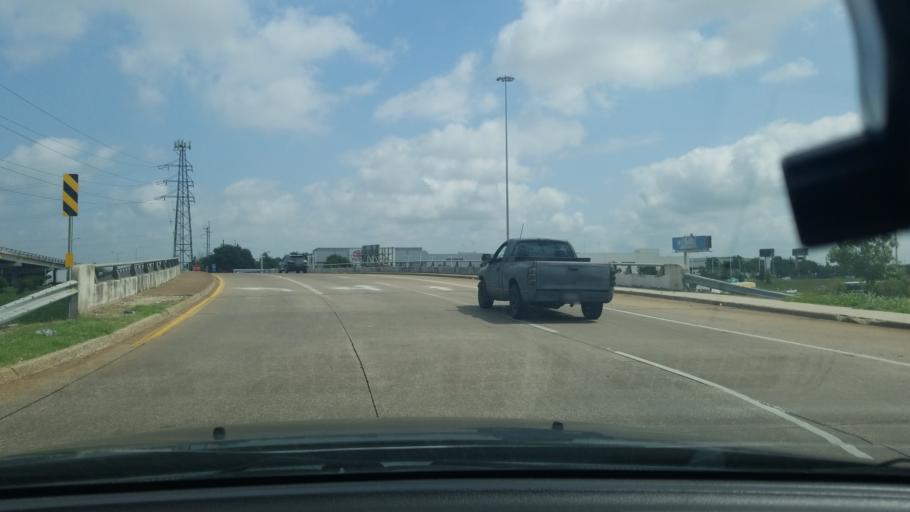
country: US
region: Texas
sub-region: Dallas County
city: Mesquite
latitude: 32.7975
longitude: -96.6819
